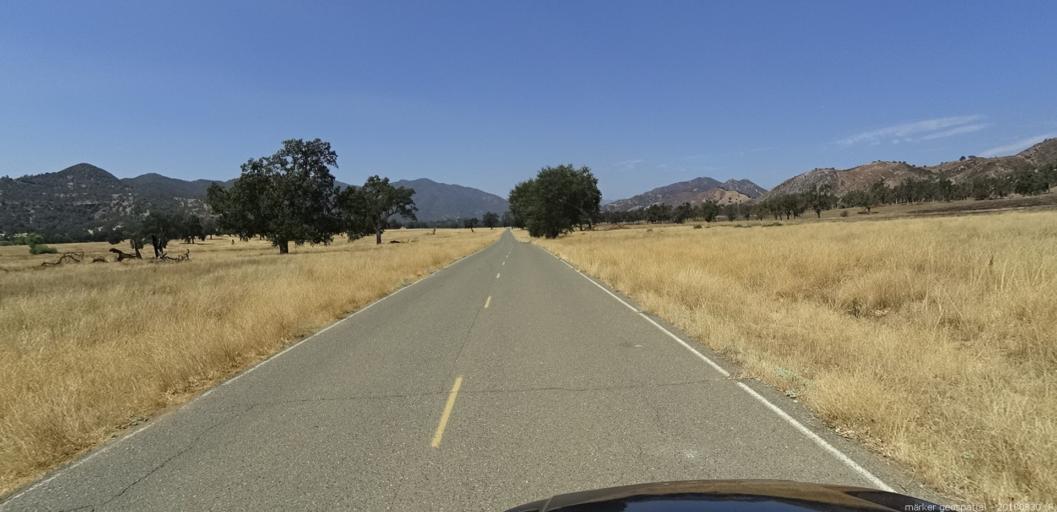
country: US
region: California
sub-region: Monterey County
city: King City
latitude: 35.9657
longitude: -121.3025
